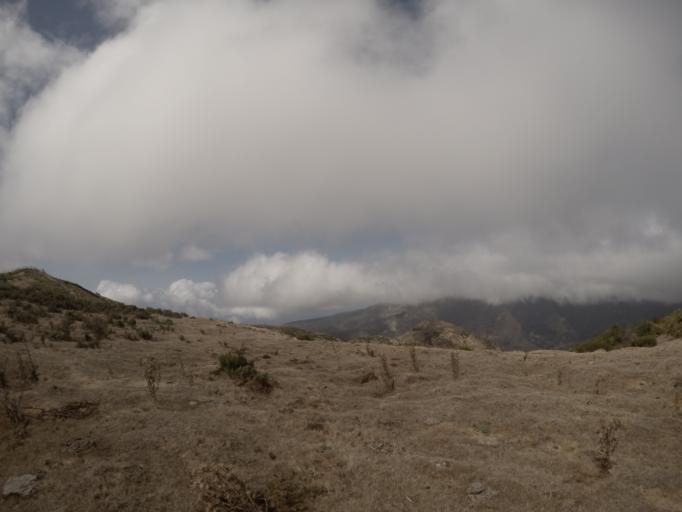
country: PT
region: Madeira
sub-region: Camara de Lobos
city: Curral das Freiras
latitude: 32.7175
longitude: -17.0003
